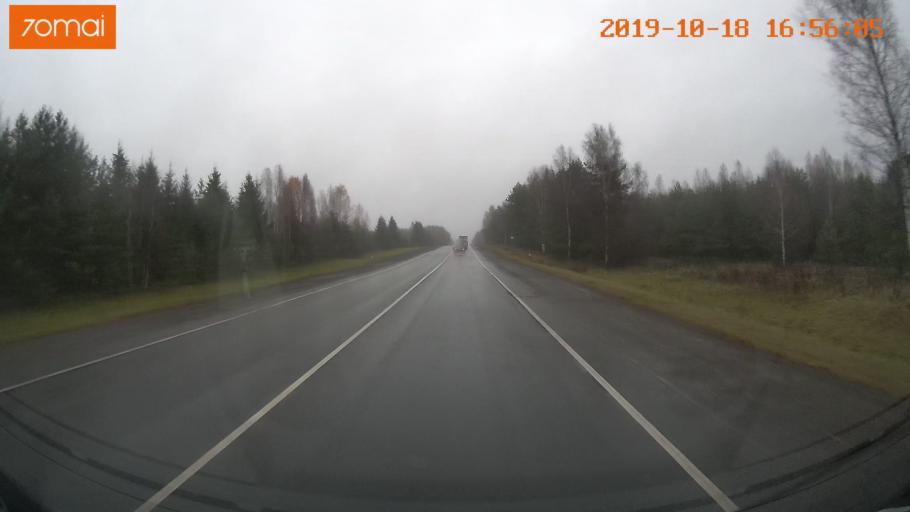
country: RU
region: Ivanovo
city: Novoye Leushino
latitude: 56.6531
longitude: 40.5855
